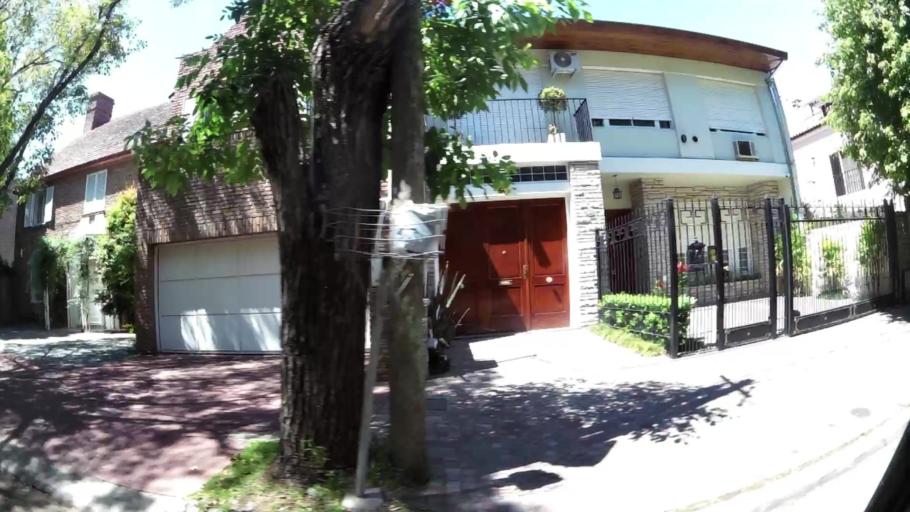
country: AR
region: Buenos Aires
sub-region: Partido de San Isidro
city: San Isidro
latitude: -34.4808
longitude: -58.4908
